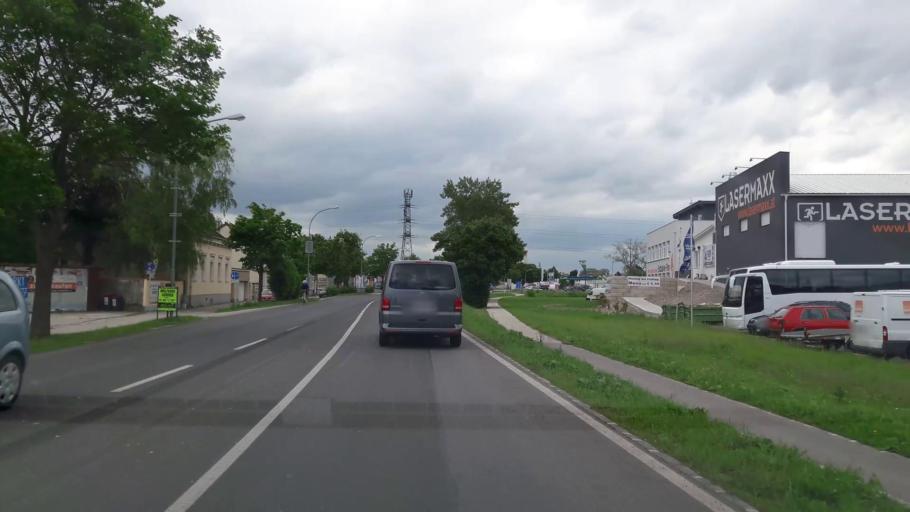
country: AT
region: Lower Austria
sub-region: Wiener Neustadt Stadt
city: Wiener Neustadt
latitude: 47.8061
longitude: 16.2647
